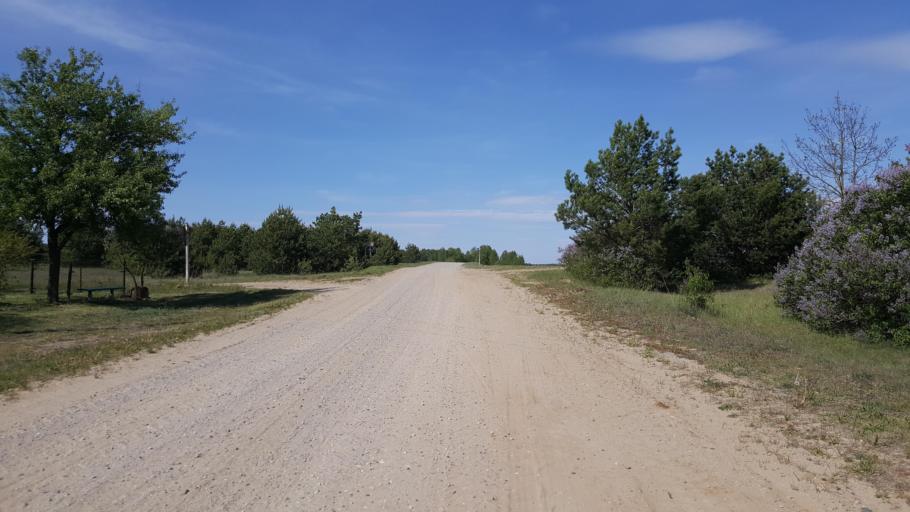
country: BY
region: Brest
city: Zhabinka
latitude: 52.3231
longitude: 24.0453
